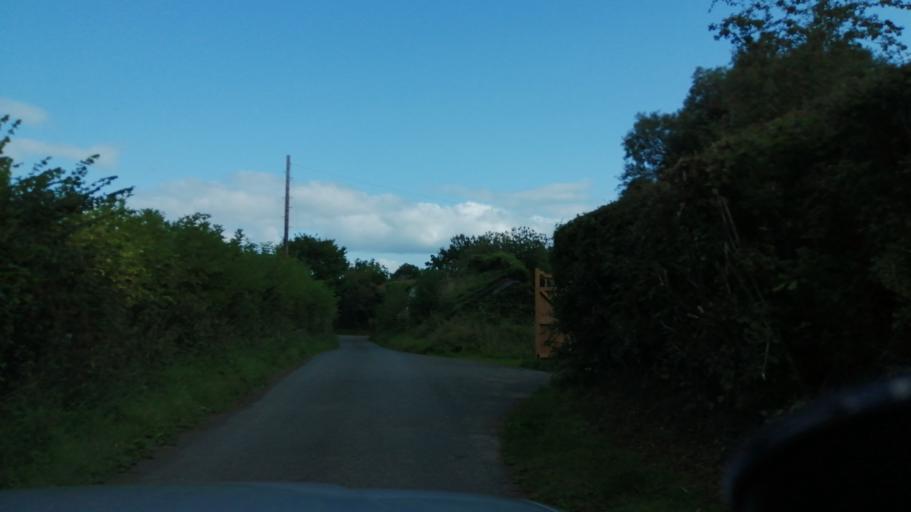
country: GB
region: England
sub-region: Herefordshire
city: Yazor
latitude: 52.1180
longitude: -2.9082
